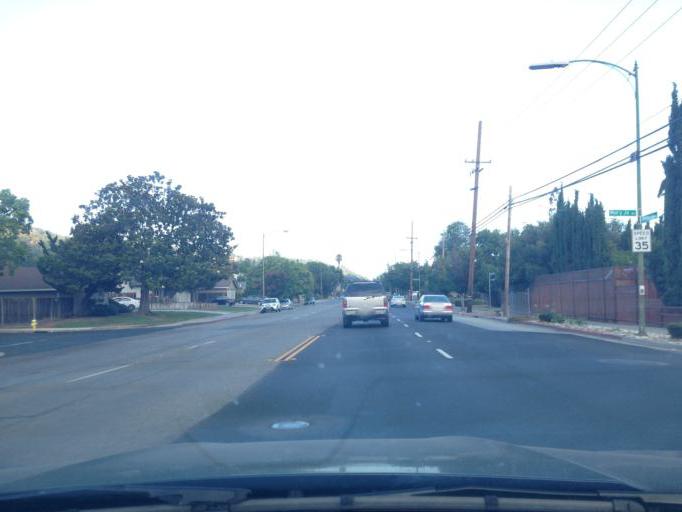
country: US
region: California
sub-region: Santa Clara County
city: Cambrian Park
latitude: 37.2363
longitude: -121.9165
